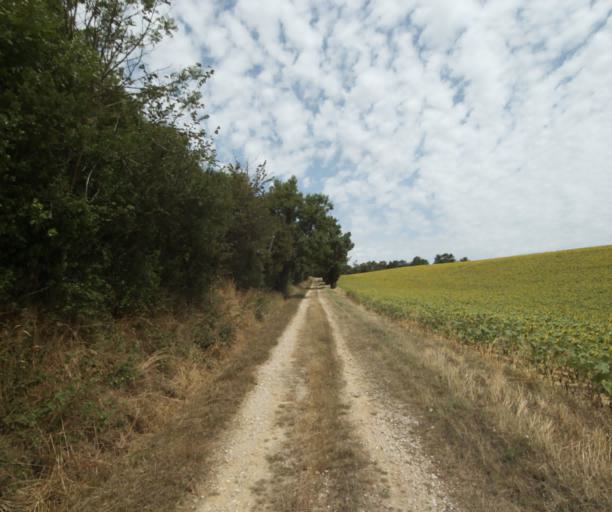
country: FR
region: Midi-Pyrenees
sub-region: Departement de la Haute-Garonne
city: Saint-Felix-Lauragais
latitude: 43.4473
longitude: 1.8920
